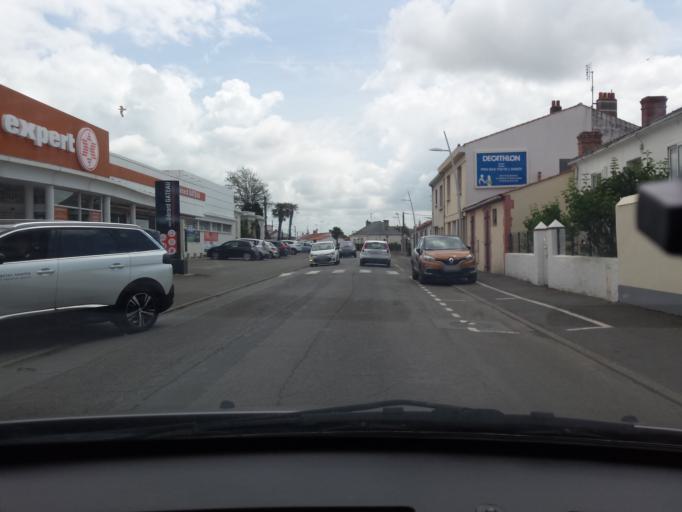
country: FR
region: Pays de la Loire
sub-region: Departement de la Vendee
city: Saint-Hilaire-de-Riez
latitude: 46.6960
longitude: -1.9274
